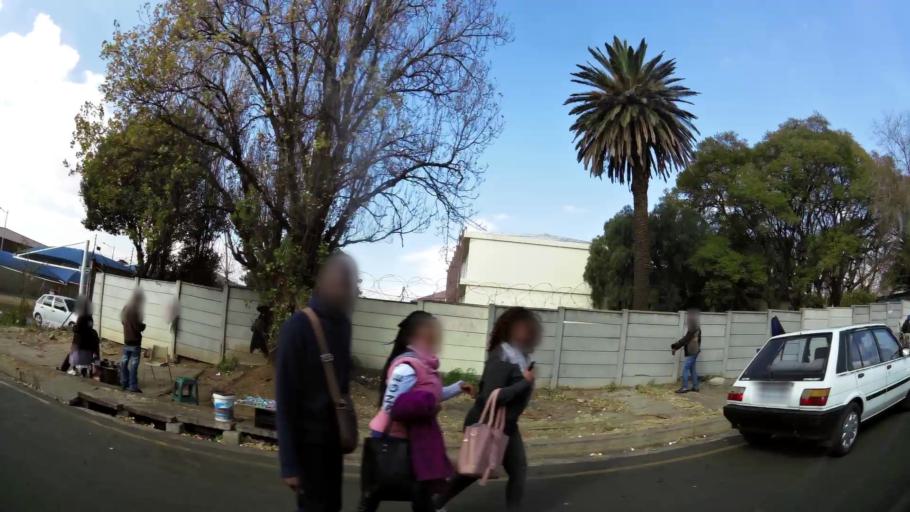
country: ZA
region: Gauteng
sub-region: West Rand District Municipality
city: Krugersdorp
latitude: -26.1077
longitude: 27.7714
